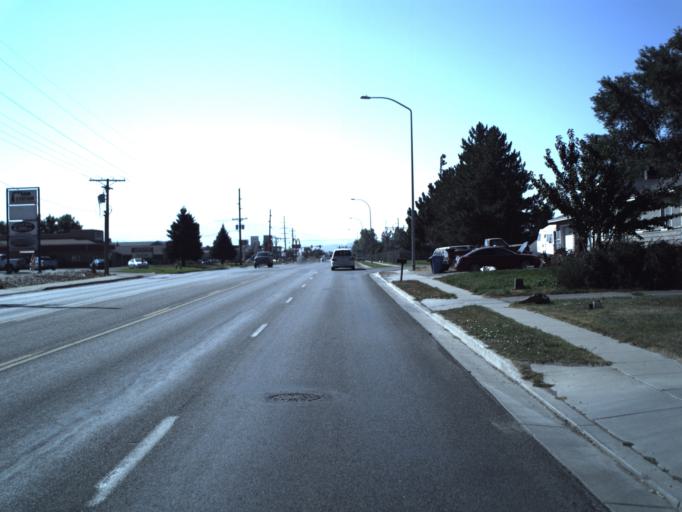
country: US
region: Utah
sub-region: Cache County
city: Hyrum
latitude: 41.6372
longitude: -111.8327
